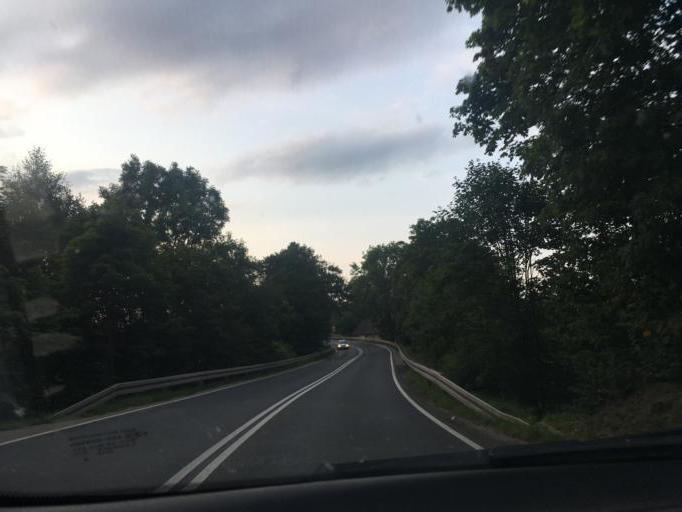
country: PL
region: Lower Silesian Voivodeship
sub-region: Powiat klodzki
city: Nowa Ruda
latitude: 50.5616
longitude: 16.5373
